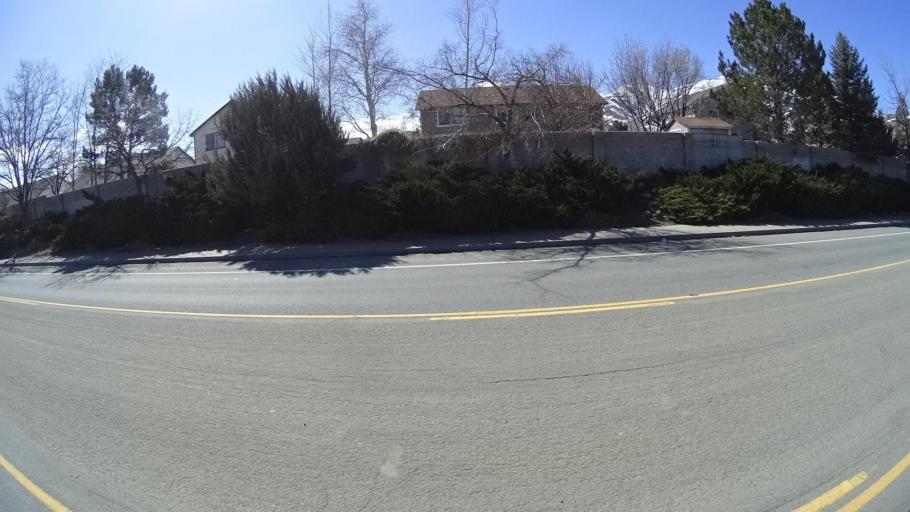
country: US
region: Nevada
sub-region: Washoe County
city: Lemmon Valley
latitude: 39.6347
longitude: -119.9043
